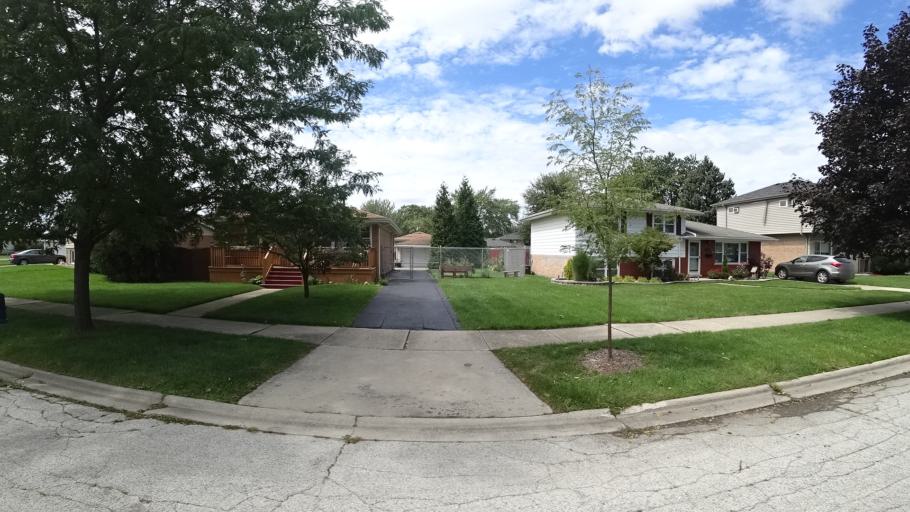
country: US
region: Illinois
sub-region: Cook County
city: Chicago Ridge
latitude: 41.7040
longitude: -87.7823
